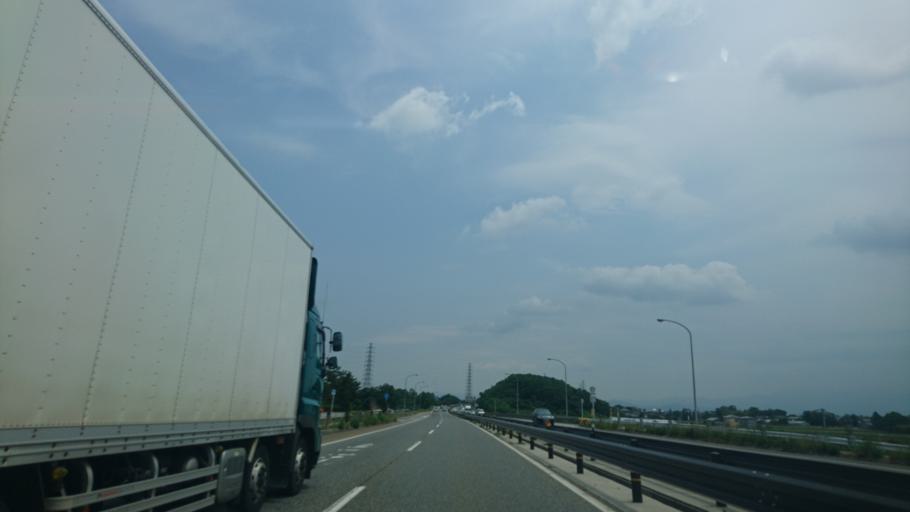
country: JP
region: Niigata
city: Suibara
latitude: 37.9536
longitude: 139.2159
